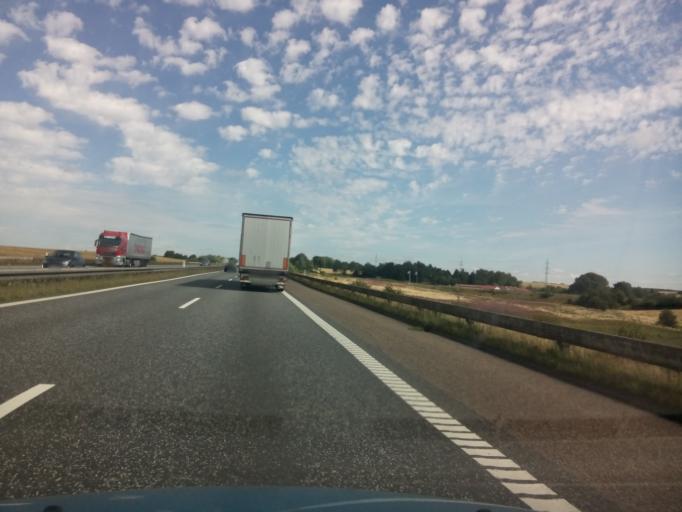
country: DK
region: Central Jutland
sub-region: Favrskov Kommune
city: Hadsten
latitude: 56.3210
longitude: 10.1206
